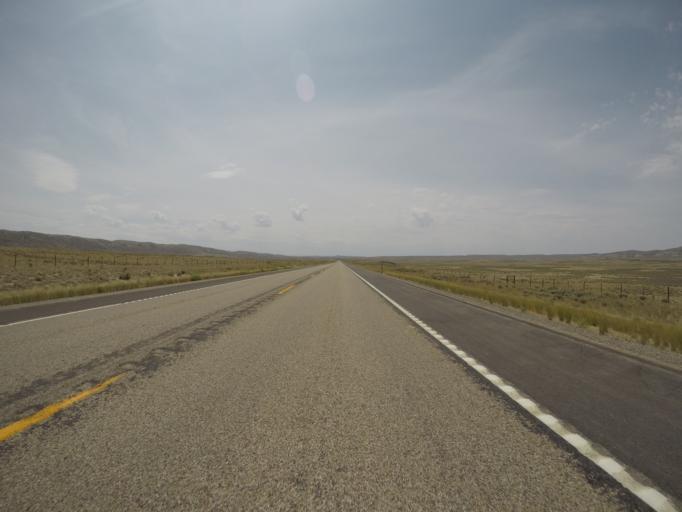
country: US
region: Wyoming
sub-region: Lincoln County
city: Kemmerer
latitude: 41.6578
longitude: -110.5704
